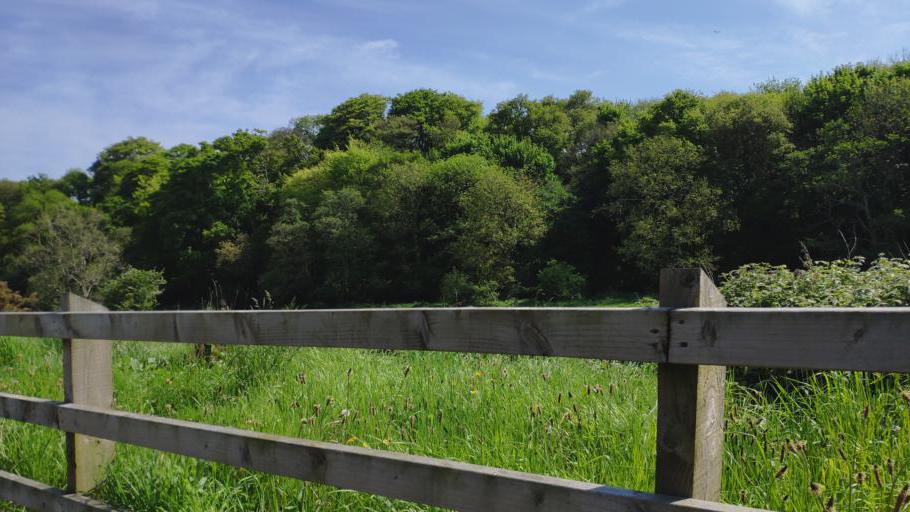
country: IE
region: Munster
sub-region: County Cork
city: Blarney
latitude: 51.9348
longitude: -8.5629
